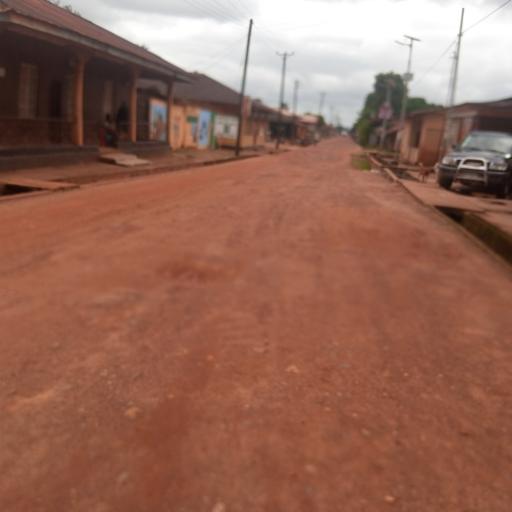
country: SL
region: Eastern Province
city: Kenema
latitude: 7.8850
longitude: -11.1875
